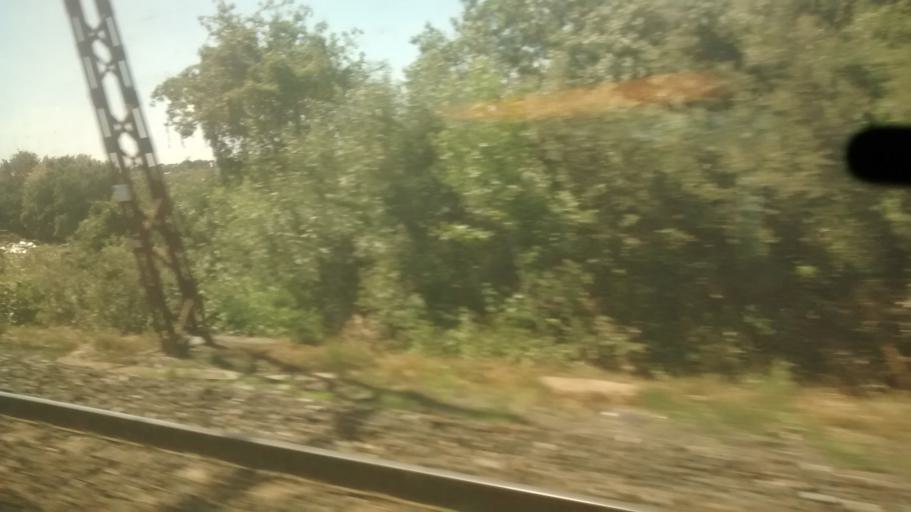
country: FR
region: Languedoc-Roussillon
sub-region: Departement de l'Herault
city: Saint-Aunes
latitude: 43.6404
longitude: 3.9793
